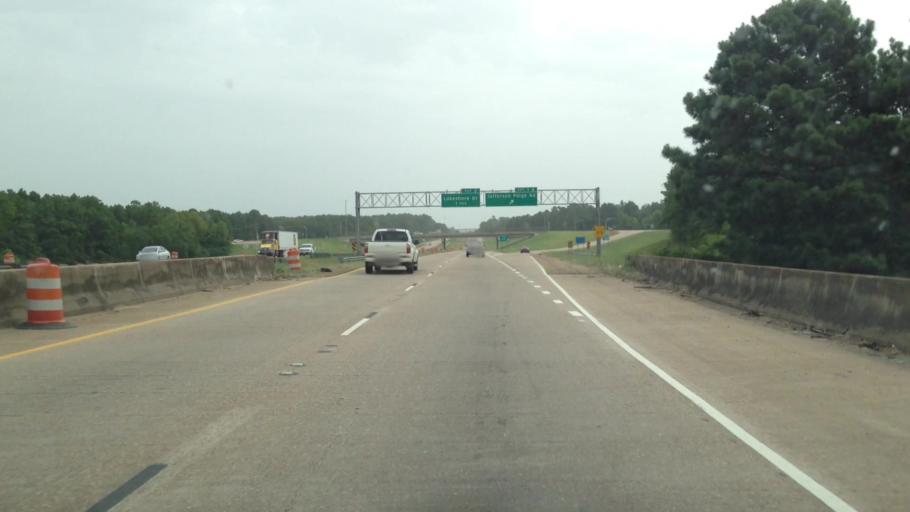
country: US
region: Louisiana
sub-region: Caddo Parish
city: Shreveport
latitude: 32.4692
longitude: -93.8400
